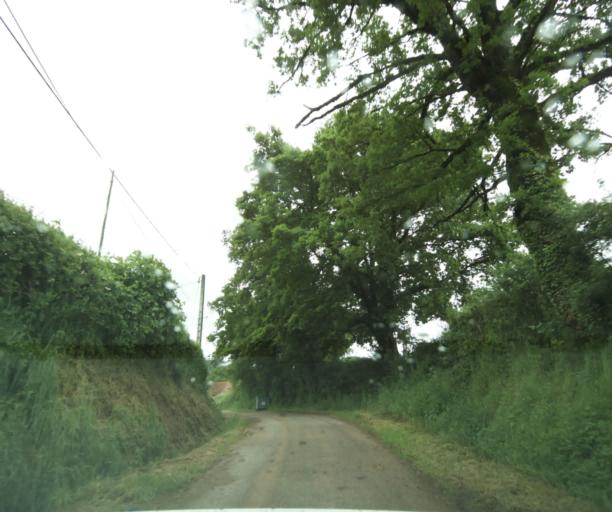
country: FR
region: Bourgogne
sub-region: Departement de Saone-et-Loire
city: Charolles
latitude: 46.4400
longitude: 4.4250
